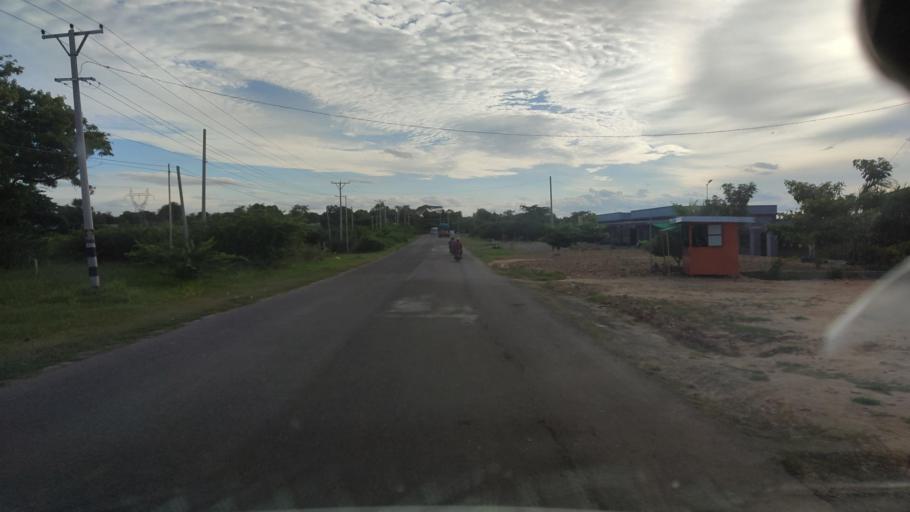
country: MM
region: Mandalay
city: Meiktila
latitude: 20.8490
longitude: 95.8135
